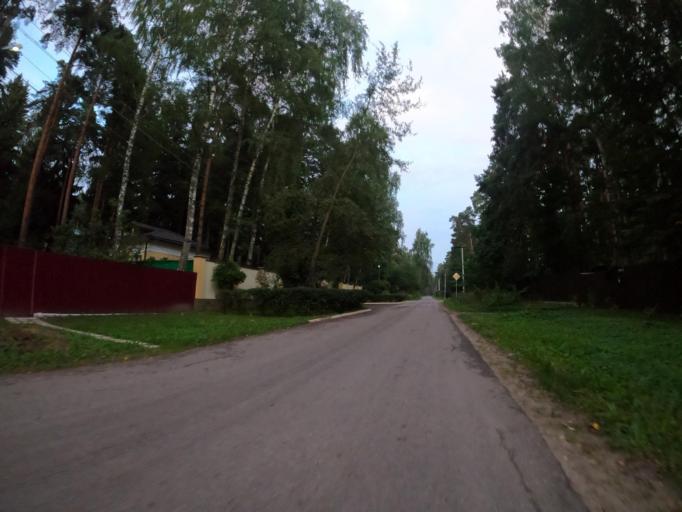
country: RU
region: Moskovskaya
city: Il'inskiy
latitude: 55.6271
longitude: 38.1013
